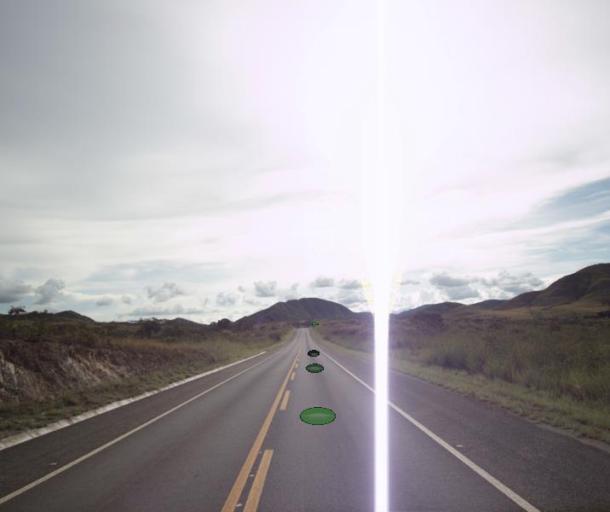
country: BR
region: Goias
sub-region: Barro Alto
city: Barro Alto
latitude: -15.1216
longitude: -48.7204
